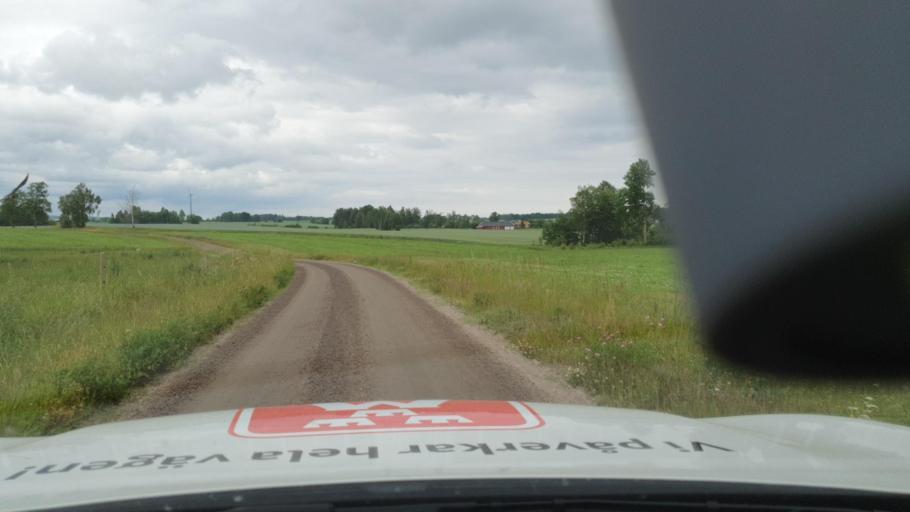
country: SE
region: Vaestra Goetaland
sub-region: Hjo Kommun
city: Hjo
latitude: 58.1844
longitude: 14.1749
